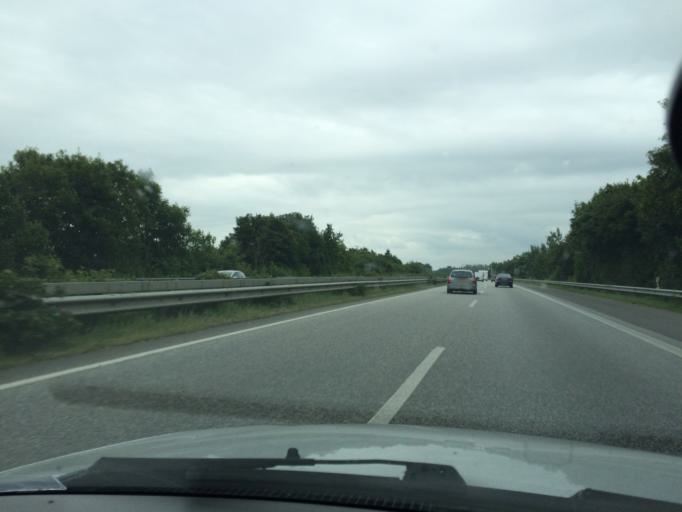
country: DE
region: Schleswig-Holstein
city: Handewitt
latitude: 54.7676
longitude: 9.3512
